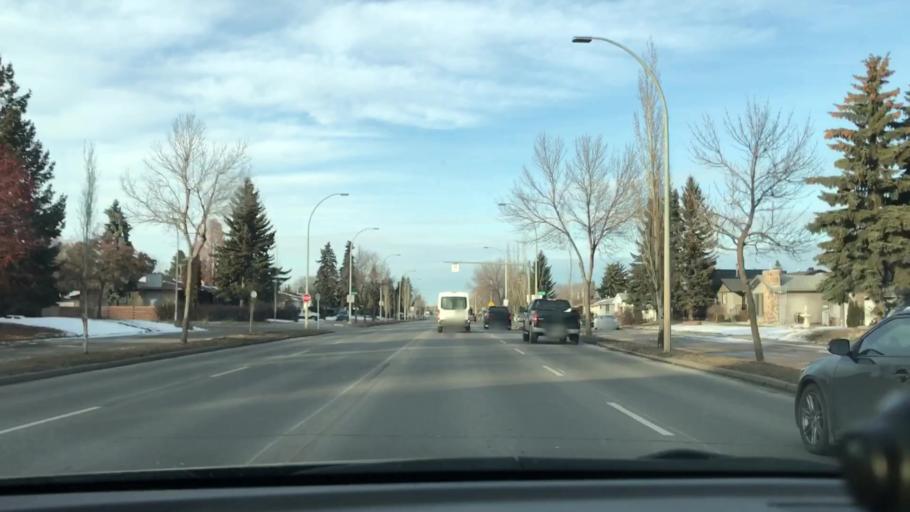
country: CA
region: Alberta
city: Edmonton
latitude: 53.5334
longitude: -113.4430
